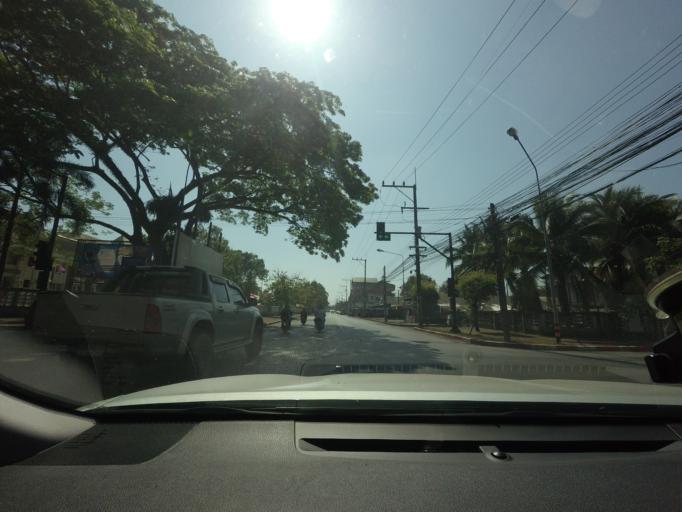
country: TH
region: Yala
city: Yala
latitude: 6.5467
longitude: 101.2864
